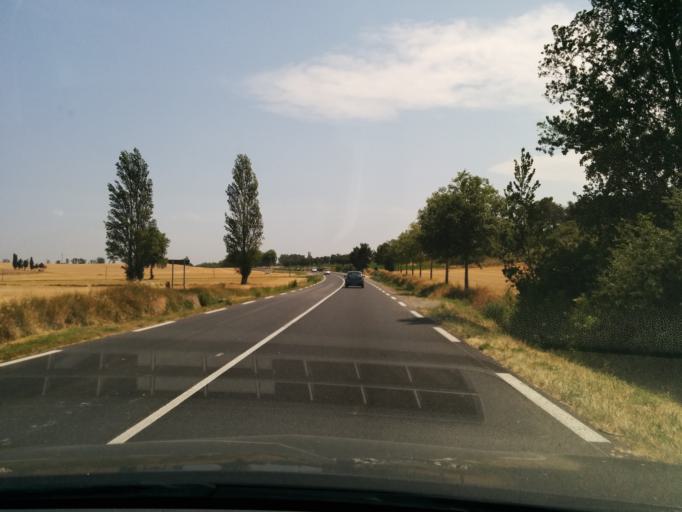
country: FR
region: Midi-Pyrenees
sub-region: Departement de la Haute-Garonne
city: Avignonet-Lauragais
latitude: 43.3544
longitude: 1.8252
